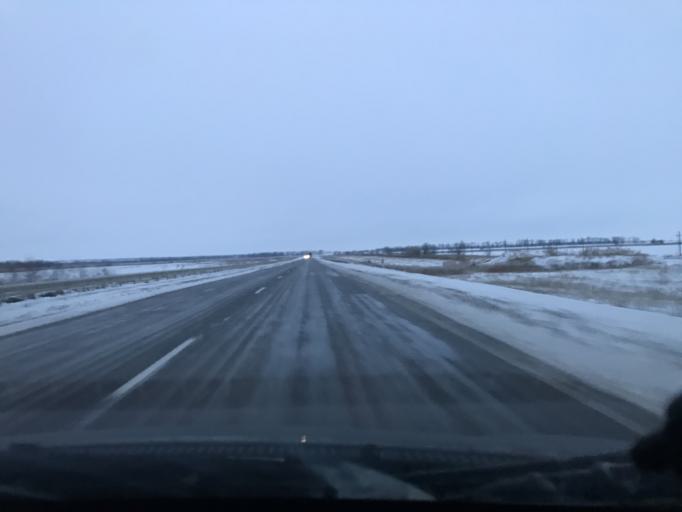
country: RU
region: Rostov
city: Letnik
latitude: 45.9633
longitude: 41.2682
